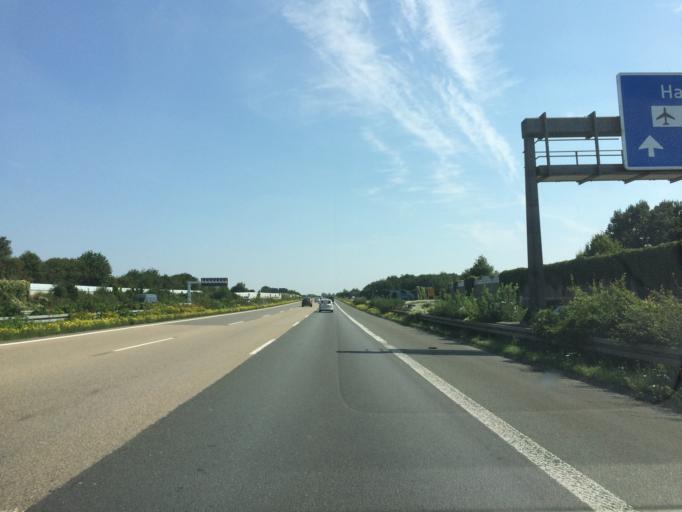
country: DE
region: North Rhine-Westphalia
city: Waltrop
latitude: 51.5842
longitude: 7.3864
